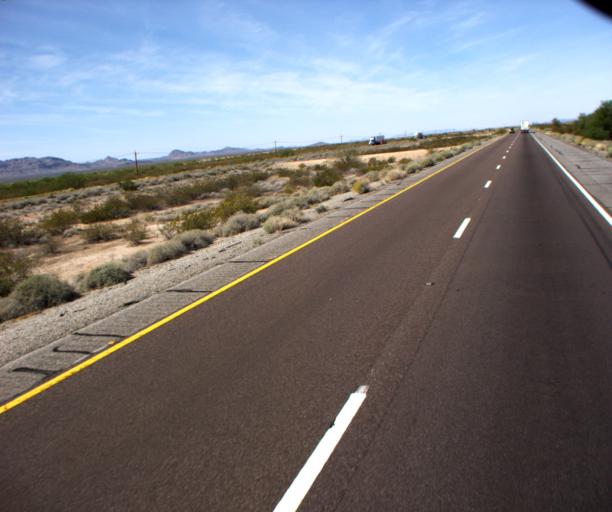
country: US
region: Arizona
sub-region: La Paz County
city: Salome
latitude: 33.5642
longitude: -113.3192
